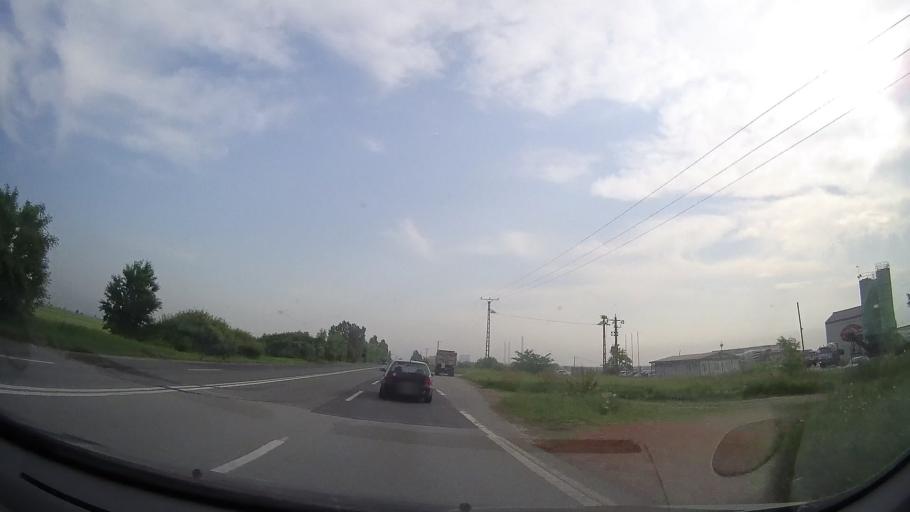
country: RO
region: Timis
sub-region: Comuna Sag
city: Sag
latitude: 45.6887
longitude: 21.1725
